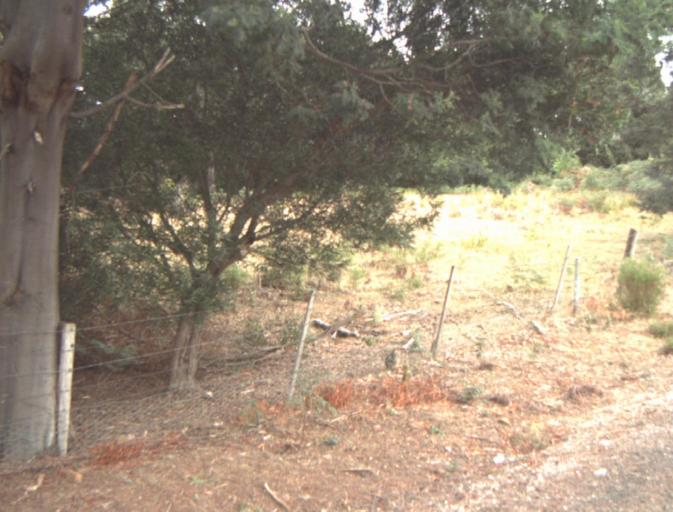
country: AU
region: Tasmania
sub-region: Launceston
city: Mayfield
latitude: -41.2858
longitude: 147.2033
